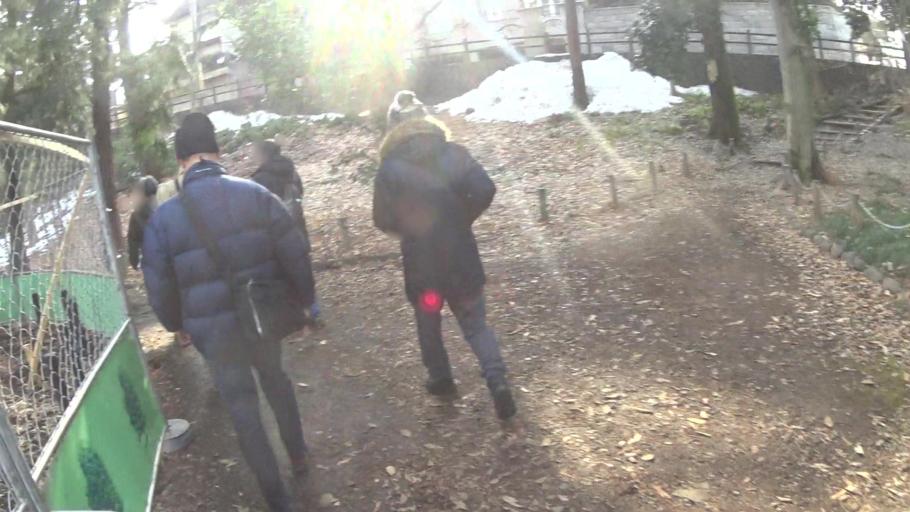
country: JP
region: Tokyo
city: Musashino
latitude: 35.7168
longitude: 139.5875
